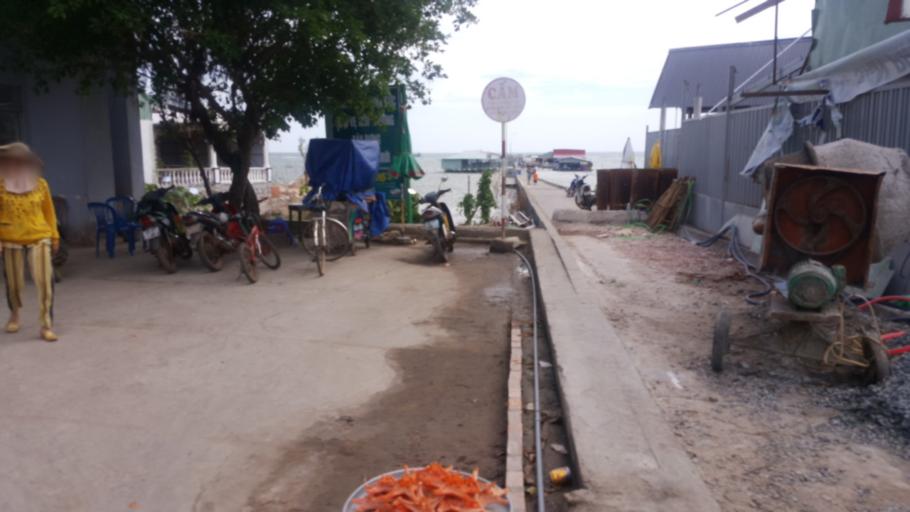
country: VN
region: Kien Giang
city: Duong GJong
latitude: 10.1812
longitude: 104.0494
